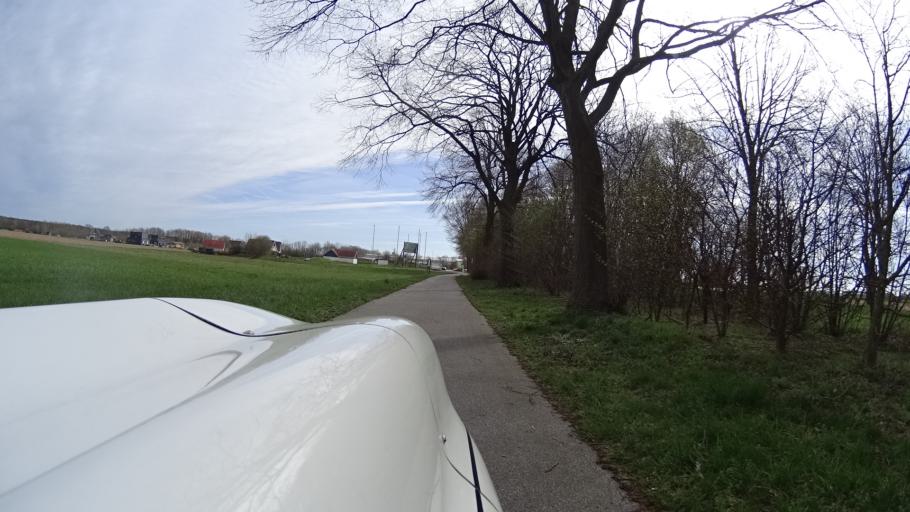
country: DE
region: North Rhine-Westphalia
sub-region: Regierungsbezirk Dusseldorf
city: Goch
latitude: 51.7035
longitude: 6.0848
